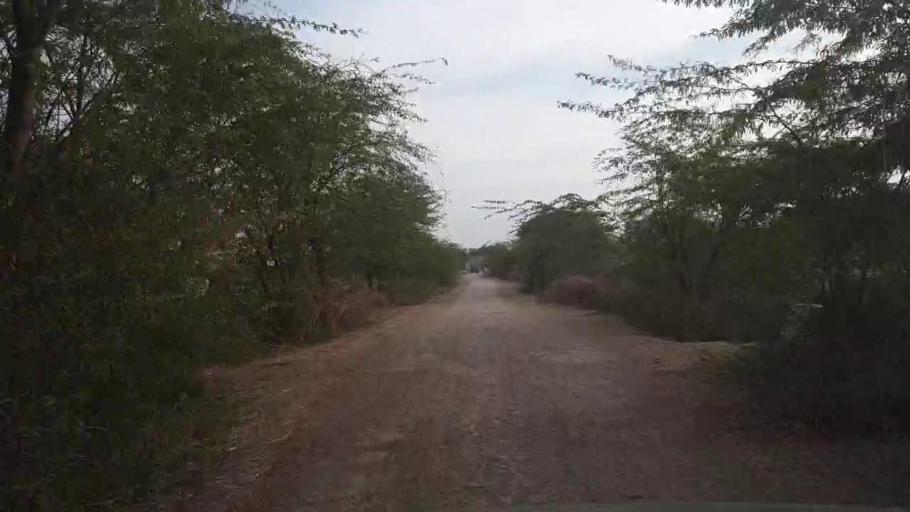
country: PK
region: Sindh
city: Shahpur Chakar
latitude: 26.1271
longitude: 68.5690
